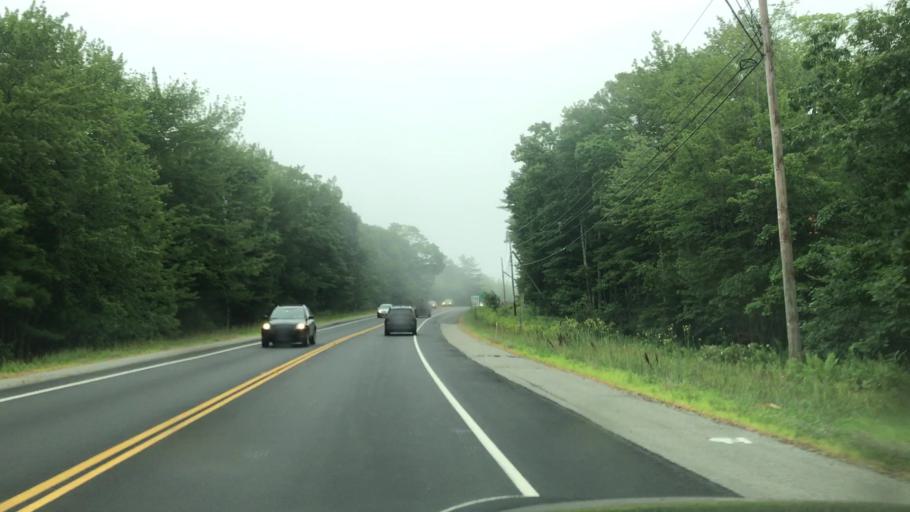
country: US
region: Maine
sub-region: Lincoln County
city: Waldoboro
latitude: 44.1086
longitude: -69.3558
